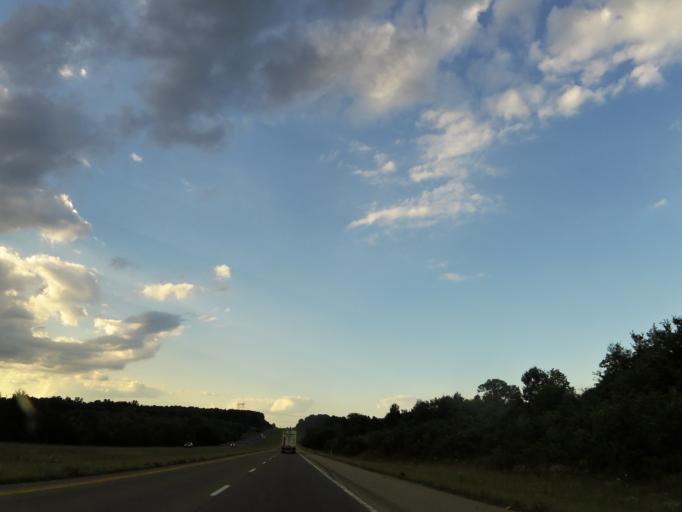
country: US
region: Tennessee
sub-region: Maury County
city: Spring Hill
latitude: 35.7026
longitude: -86.8822
